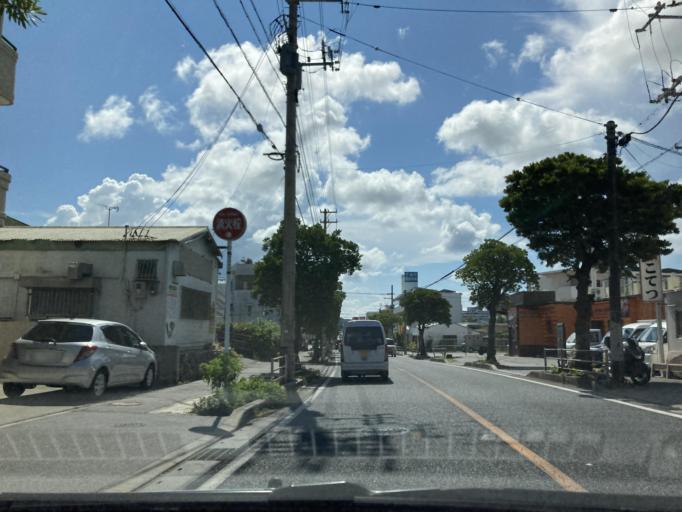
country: JP
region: Okinawa
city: Tomigusuku
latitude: 26.1849
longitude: 127.7120
